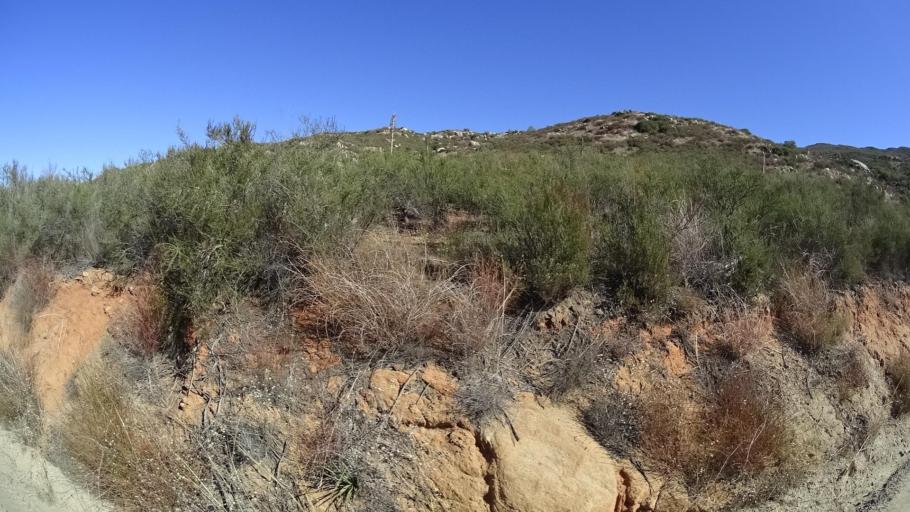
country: US
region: California
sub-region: San Diego County
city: Descanso
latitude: 32.8632
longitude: -116.6916
